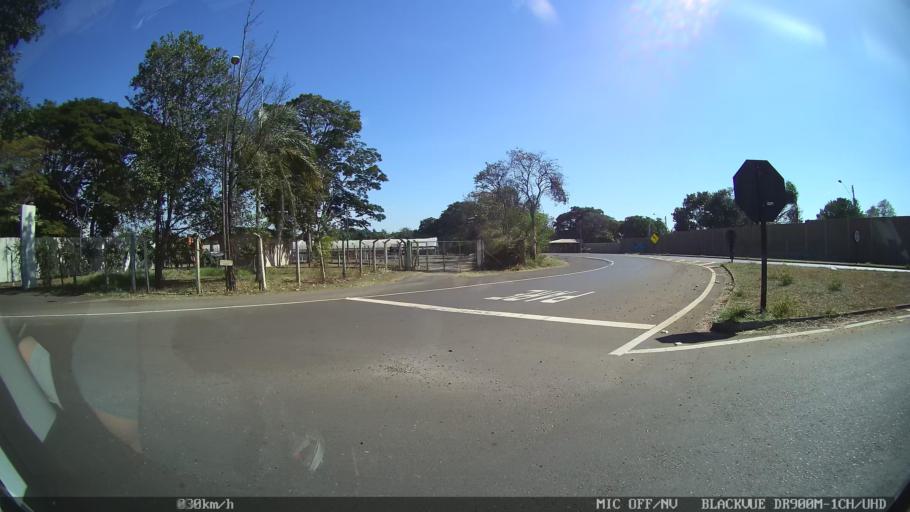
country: BR
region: Sao Paulo
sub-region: Franca
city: Franca
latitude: -20.4595
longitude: -47.4168
